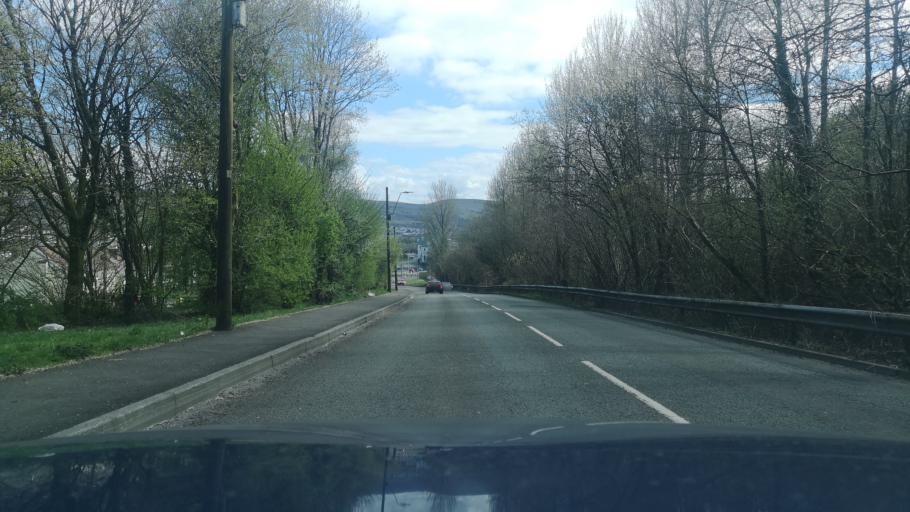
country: GB
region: Wales
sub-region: Merthyr Tydfil County Borough
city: Merthyr Tydfil
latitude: 51.7522
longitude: -3.4055
